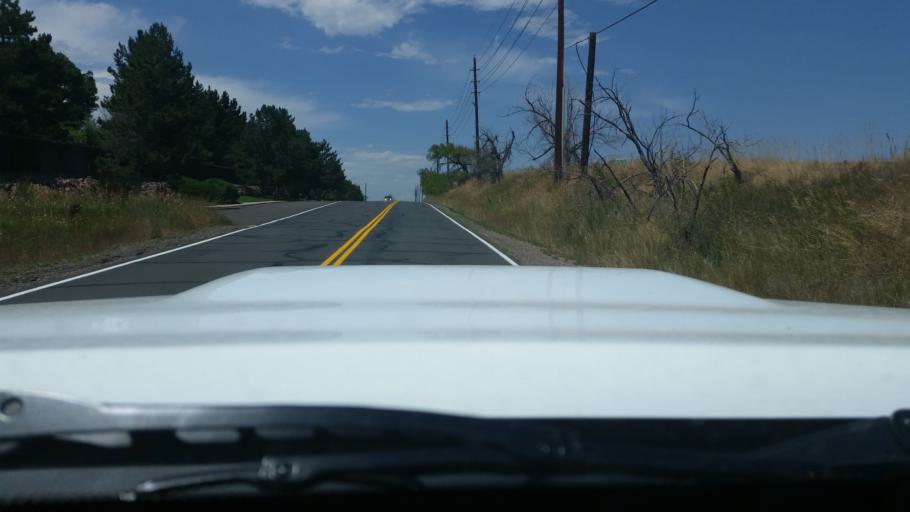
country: US
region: Colorado
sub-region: Broomfield County
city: Broomfield
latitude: 39.8940
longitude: -105.0811
